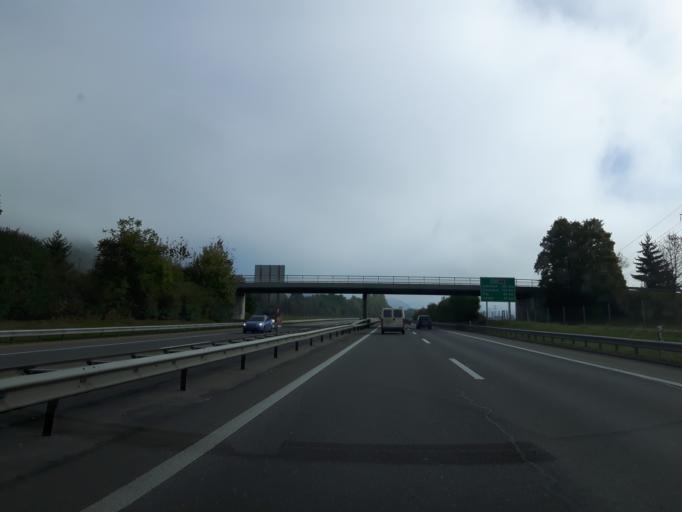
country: CH
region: Lucerne
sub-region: Willisau District
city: Reiden
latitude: 47.2373
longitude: 7.9623
